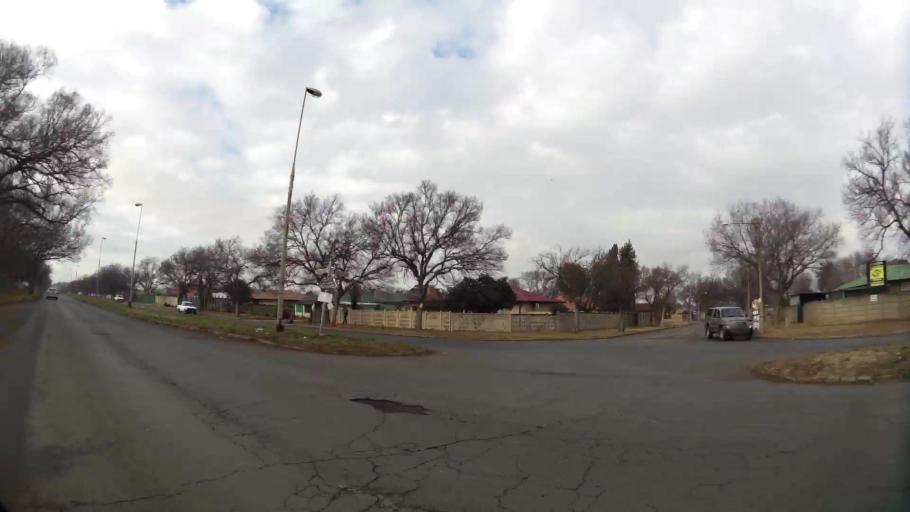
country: ZA
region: Gauteng
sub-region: Sedibeng District Municipality
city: Vanderbijlpark
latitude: -26.6926
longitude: 27.8153
